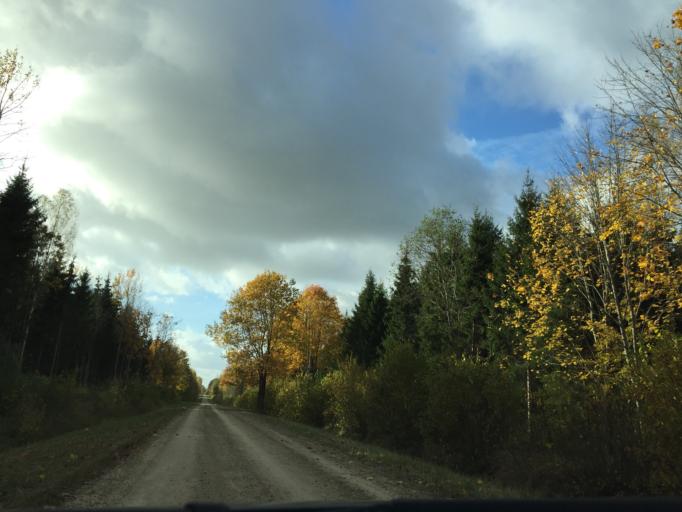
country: LV
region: Ogre
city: Jumprava
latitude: 56.7397
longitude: 24.9389
